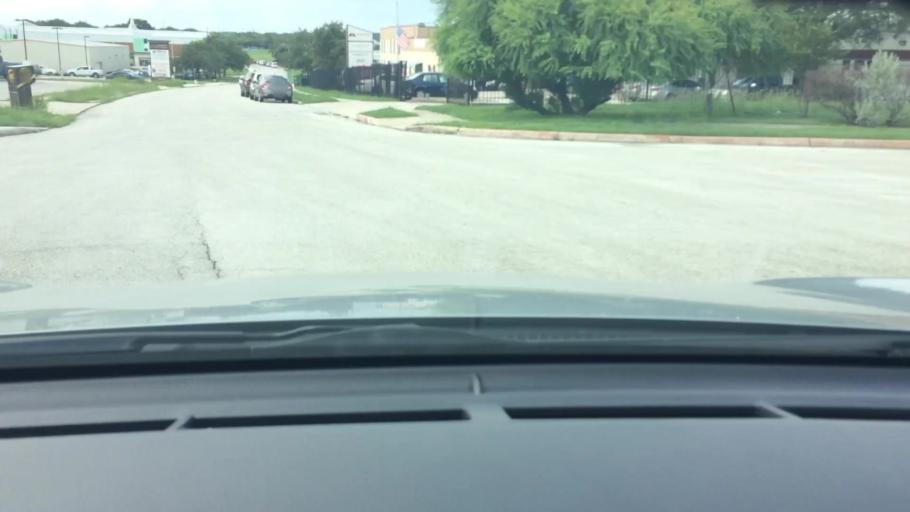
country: US
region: Texas
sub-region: Bexar County
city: Leon Valley
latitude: 29.5319
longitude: -98.5866
